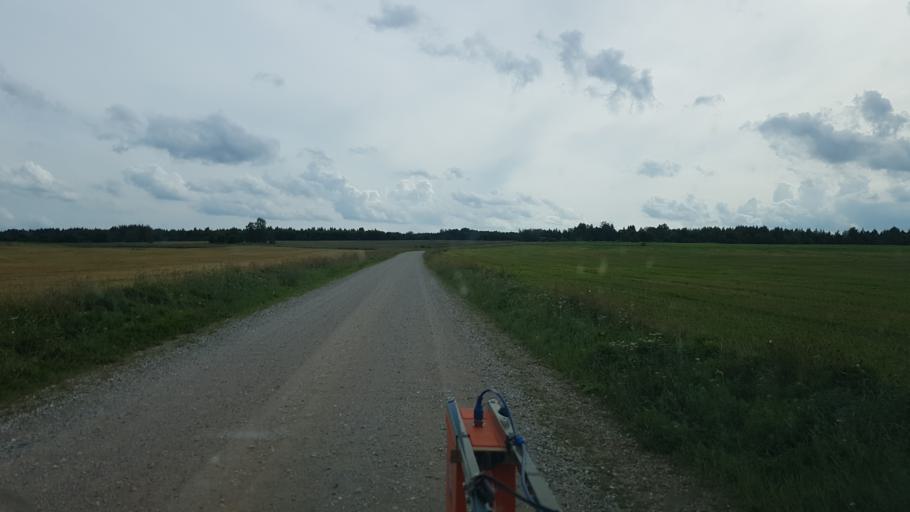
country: RU
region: Pskov
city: Pechory
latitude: 57.8045
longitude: 27.5072
